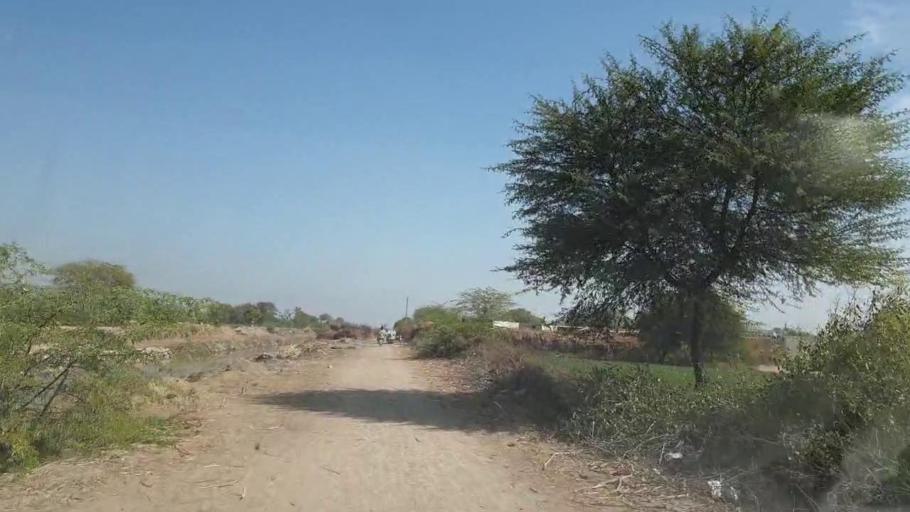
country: PK
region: Sindh
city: Mirpur Khas
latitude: 25.5412
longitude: 69.1609
